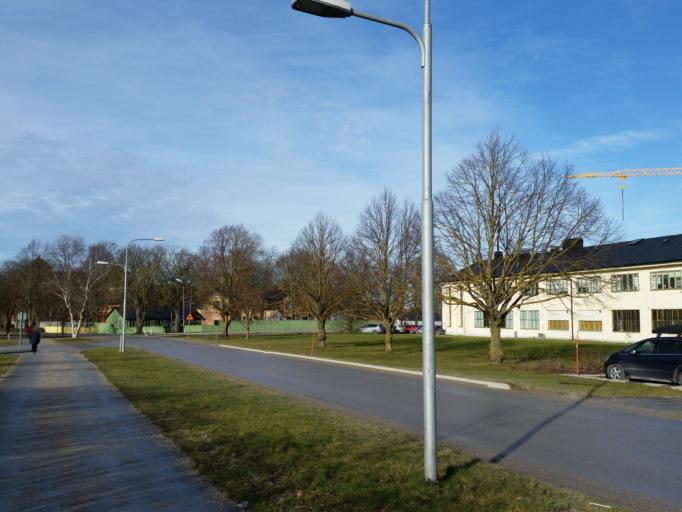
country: SE
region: Gotland
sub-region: Gotland
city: Visby
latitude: 57.6307
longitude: 18.3044
